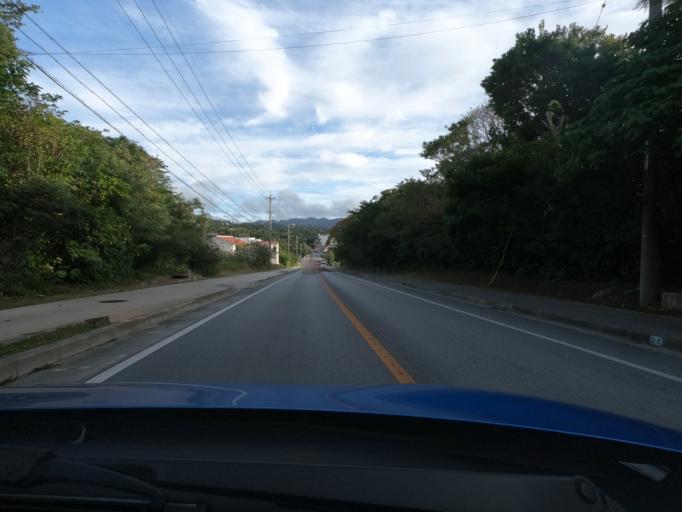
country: JP
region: Okinawa
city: Nago
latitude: 26.6803
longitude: 127.8867
